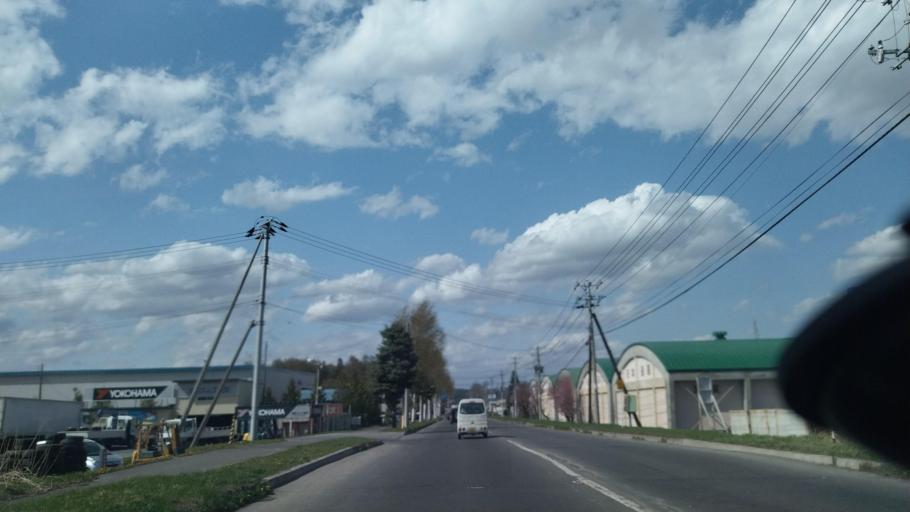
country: JP
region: Hokkaido
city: Obihiro
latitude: 42.9251
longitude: 143.1435
